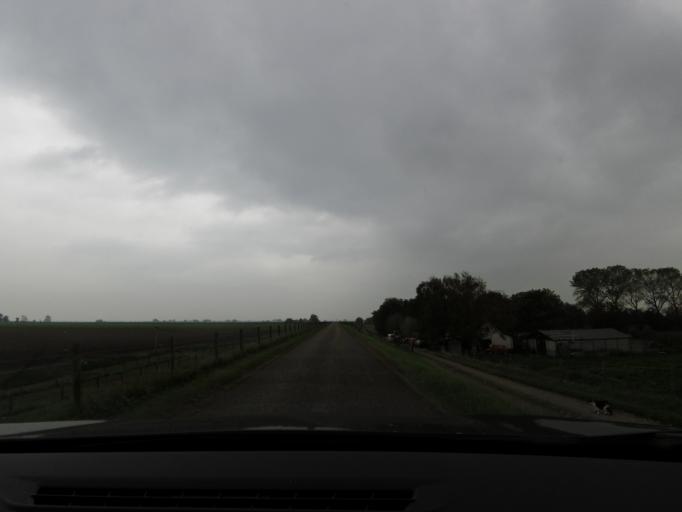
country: NL
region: South Holland
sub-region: Gemeente Spijkenisse
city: Spijkenisse
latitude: 51.8022
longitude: 4.2495
